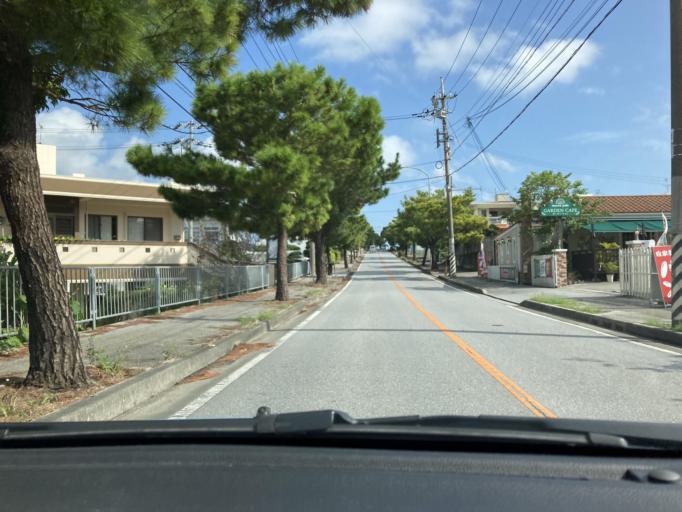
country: JP
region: Okinawa
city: Ginowan
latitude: 26.2646
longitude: 127.7749
